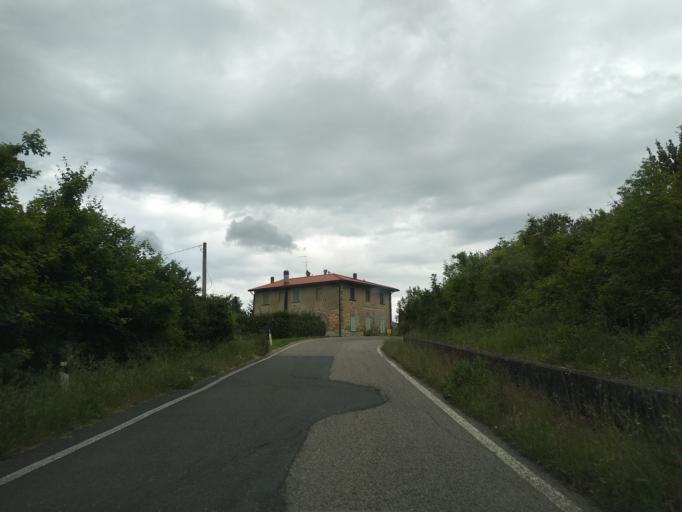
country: IT
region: Tuscany
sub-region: Provincia di Livorno
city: Collesalvetti
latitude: 43.5397
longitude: 10.4395
